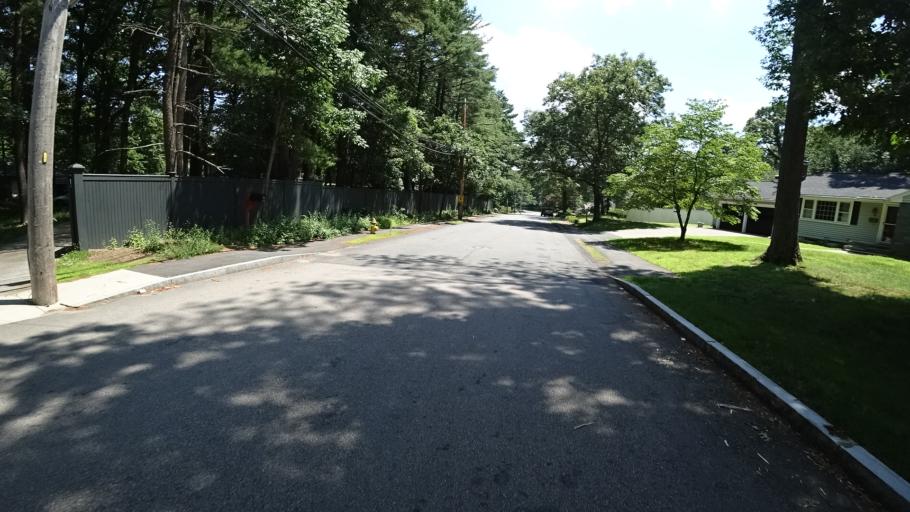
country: US
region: Massachusetts
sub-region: Norfolk County
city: Dedham
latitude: 42.2455
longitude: -71.1984
